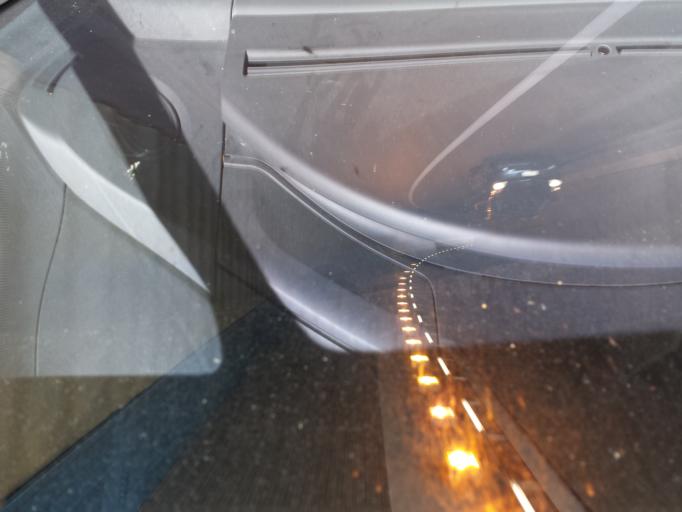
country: DE
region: Baden-Wuerttemberg
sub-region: Freiburg Region
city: Konstanz
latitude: 47.6519
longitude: 9.1722
